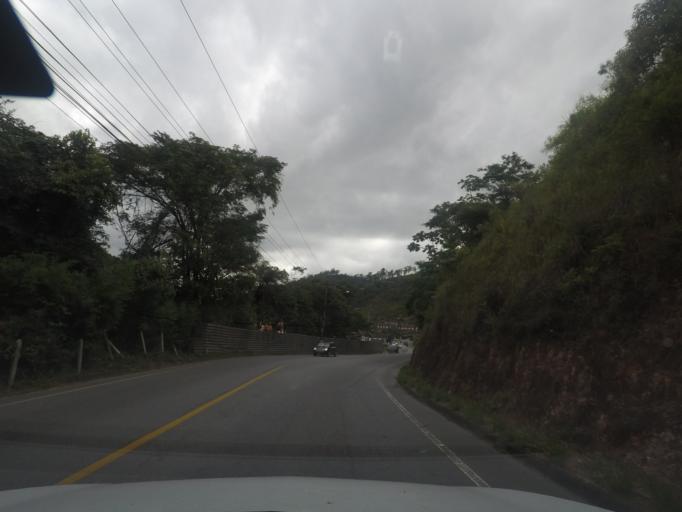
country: BR
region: Rio de Janeiro
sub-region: Teresopolis
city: Teresopolis
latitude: -22.3882
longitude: -42.9571
